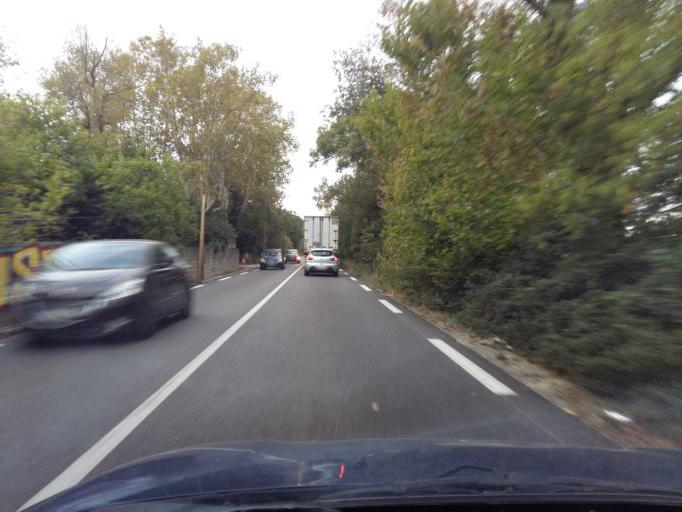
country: FR
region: Provence-Alpes-Cote d'Azur
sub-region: Departement des Bouches-du-Rhone
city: Miramas
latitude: 43.6124
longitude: 5.0116
